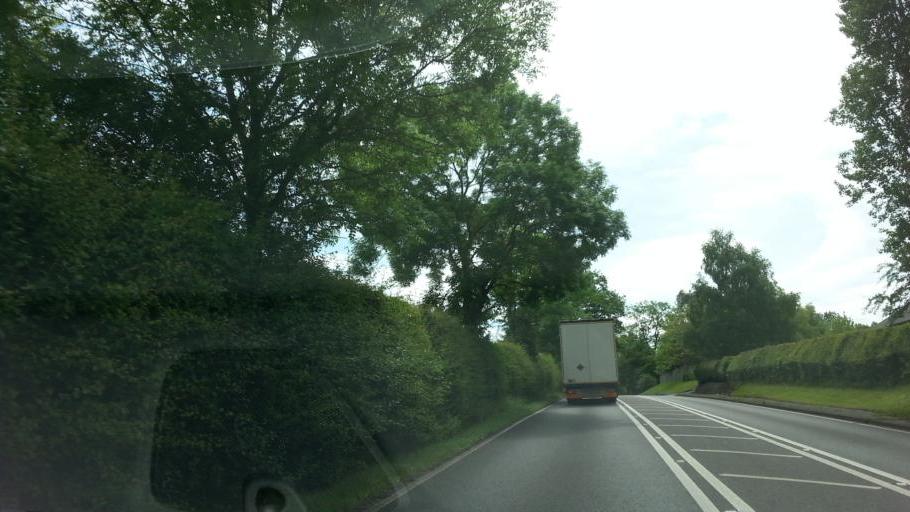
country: GB
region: England
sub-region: Nottinghamshire
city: Cotgrave
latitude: 52.8762
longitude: -1.0549
